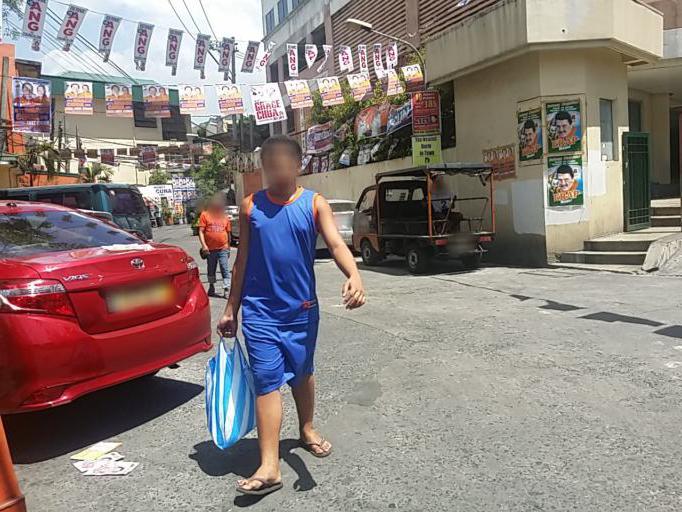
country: PH
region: Metro Manila
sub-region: City of Manila
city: Quiapo
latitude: 14.6008
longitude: 120.9866
